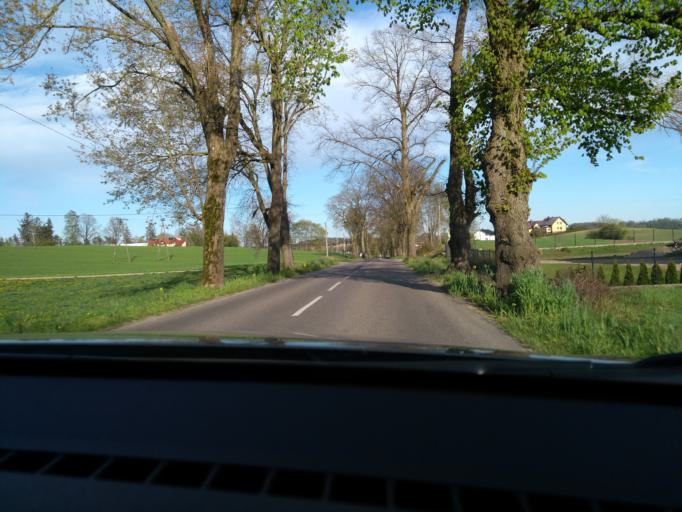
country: PL
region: Pomeranian Voivodeship
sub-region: Powiat kartuski
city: Suleczyno
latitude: 54.3281
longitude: 17.7790
